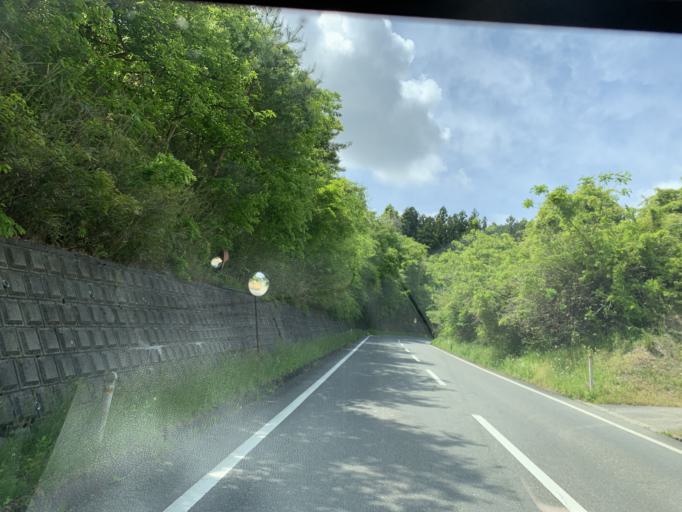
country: JP
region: Iwate
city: Ichinoseki
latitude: 38.7789
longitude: 140.9973
